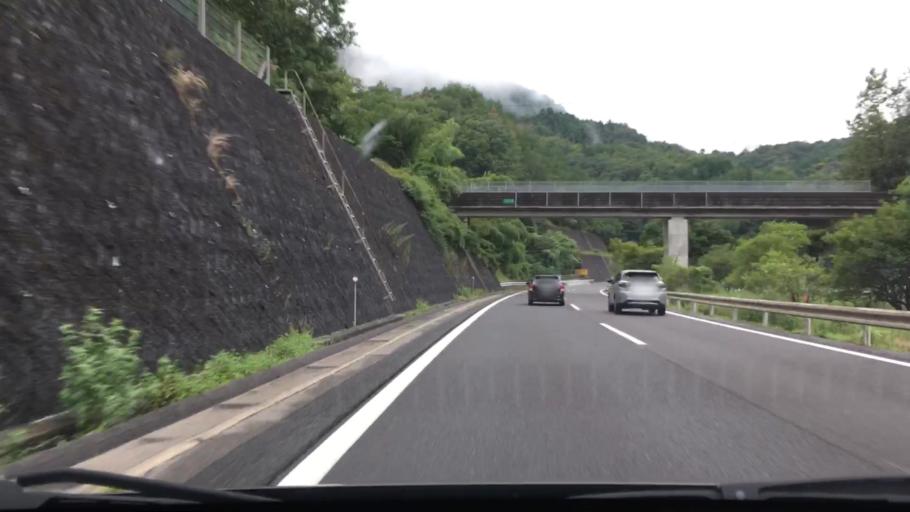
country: JP
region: Hiroshima
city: Hiroshima-shi
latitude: 34.5455
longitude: 132.4520
